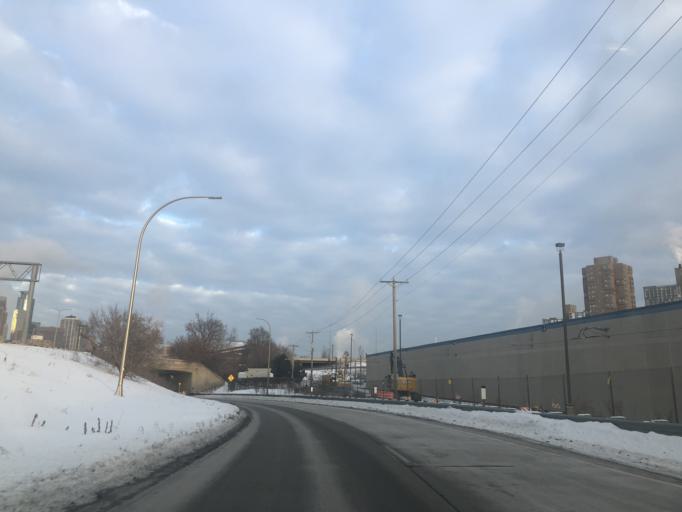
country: US
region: Minnesota
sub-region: Hennepin County
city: Minneapolis
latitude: 44.9640
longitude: -93.2500
